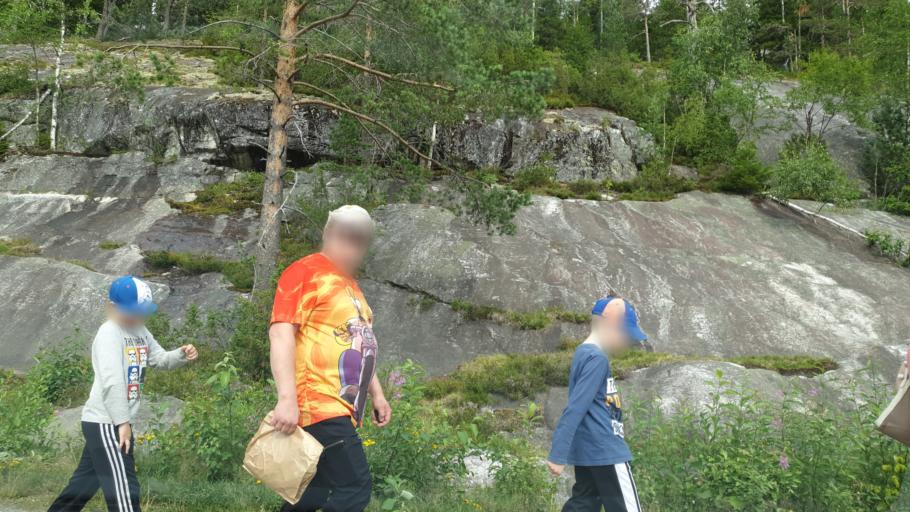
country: FI
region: North Karelia
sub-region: Pielisen Karjala
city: Lieksa
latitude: 63.0949
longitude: 29.8038
